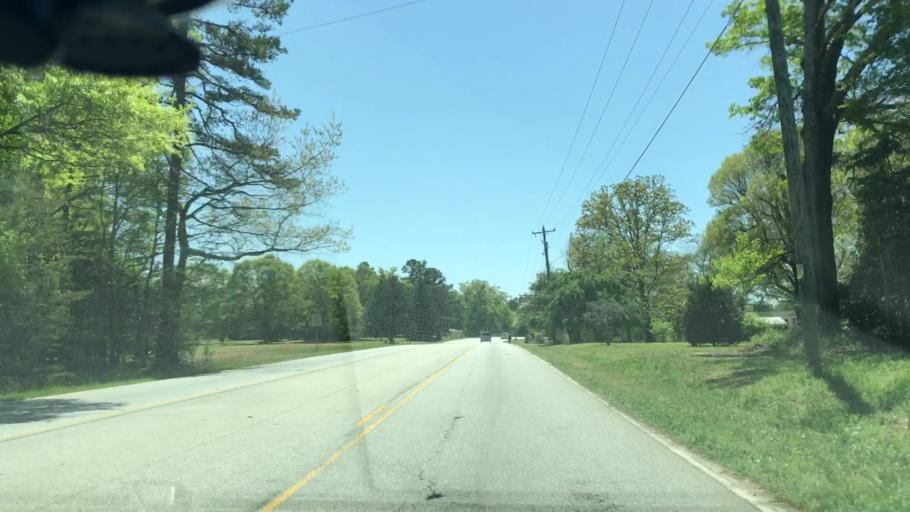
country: US
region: South Carolina
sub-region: Greenville County
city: Mauldin
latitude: 34.7475
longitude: -82.2913
